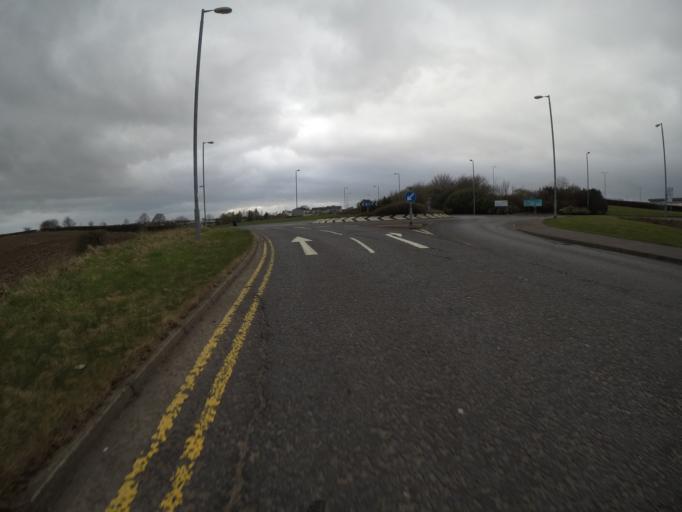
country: GB
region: Scotland
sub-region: East Ayrshire
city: Crosshouse
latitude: 55.6122
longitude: -4.5408
